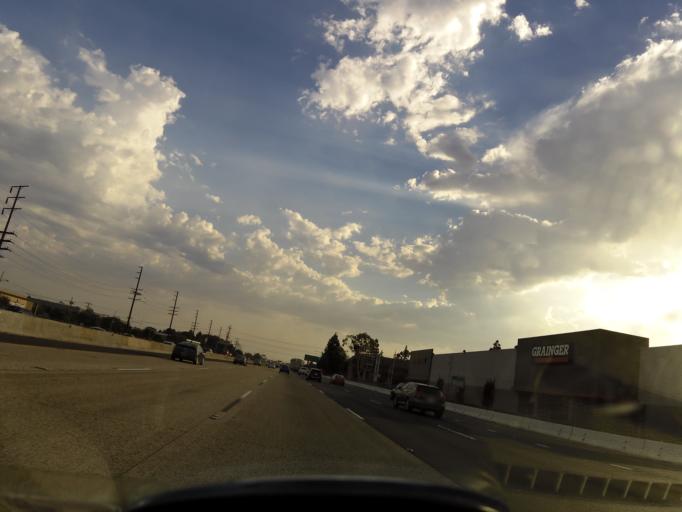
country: US
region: California
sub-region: Orange County
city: Tustin
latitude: 33.7145
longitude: -117.8461
